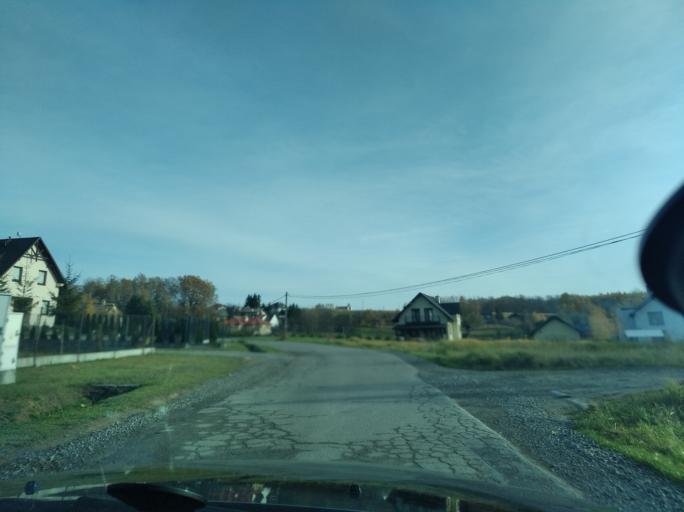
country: PL
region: Subcarpathian Voivodeship
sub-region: Powiat rzeszowski
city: Krasne
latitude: 50.0149
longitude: 22.0988
